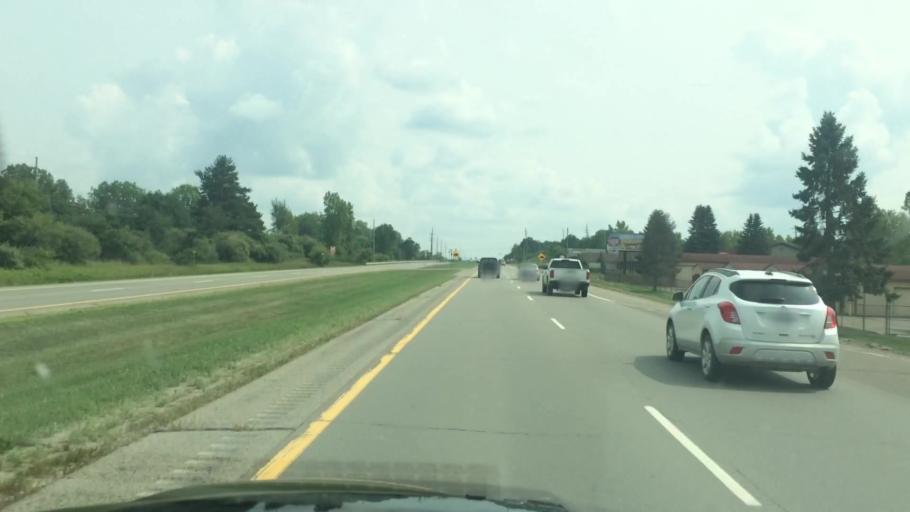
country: US
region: Michigan
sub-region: Oakland County
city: Oxford
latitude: 42.8525
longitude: -83.2832
